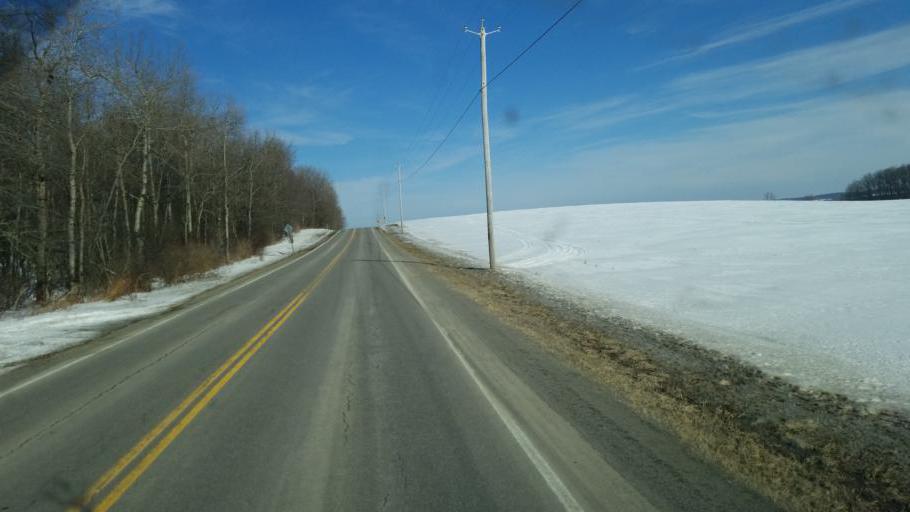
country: US
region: New York
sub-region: Allegany County
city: Andover
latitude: 42.1155
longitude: -77.7827
